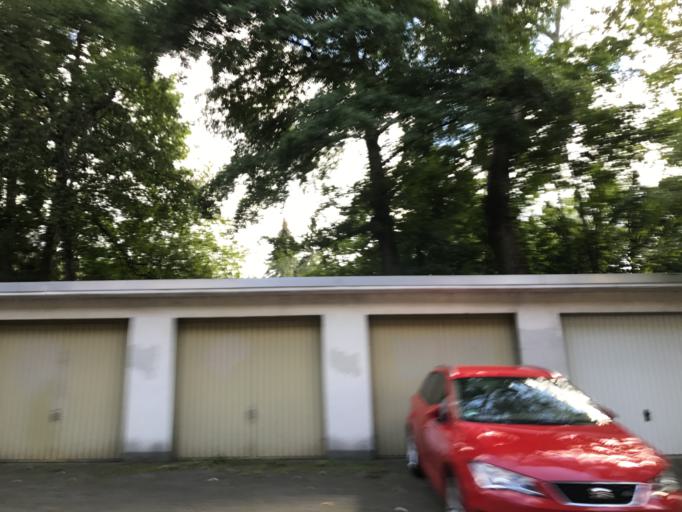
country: DE
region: Lower Saxony
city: Bad Harzburg
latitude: 51.8846
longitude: 10.5716
